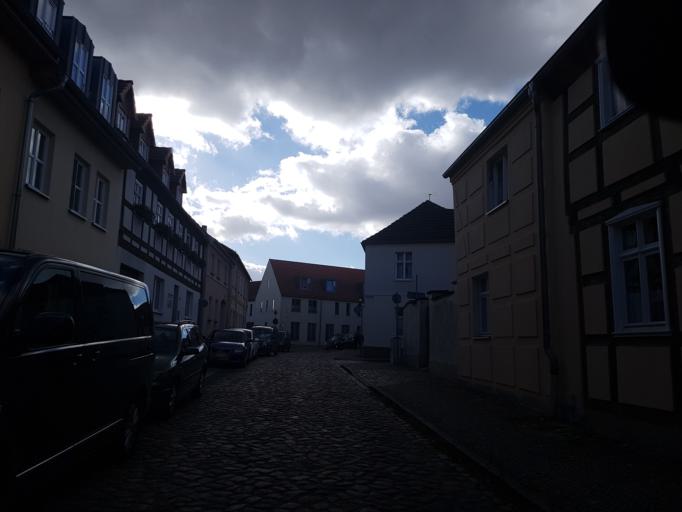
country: DE
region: Brandenburg
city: Nauen
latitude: 52.6068
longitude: 12.8792
